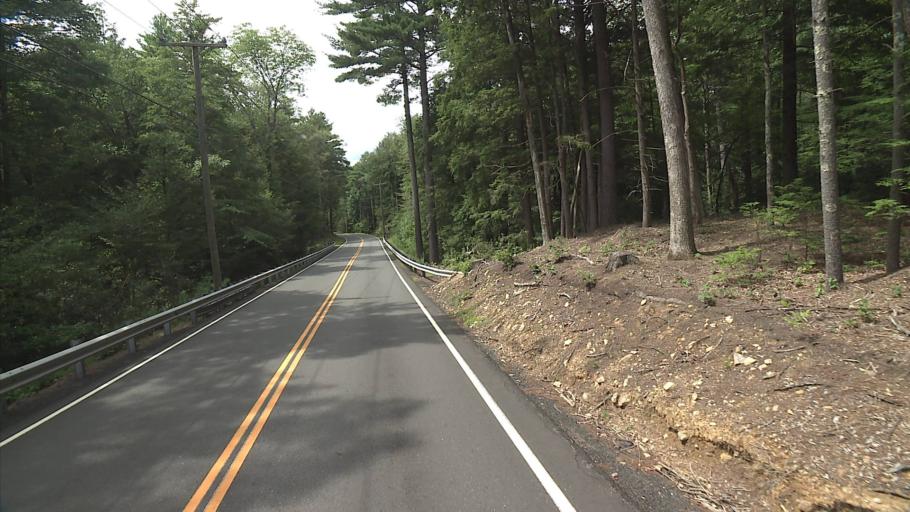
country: US
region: Massachusetts
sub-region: Hampden County
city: Holland
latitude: 41.9932
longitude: -72.1432
